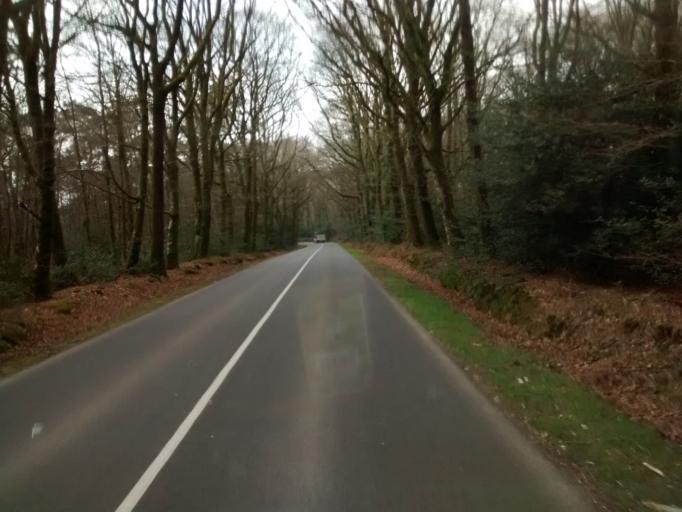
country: FR
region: Brittany
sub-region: Departement d'Ille-et-Vilaine
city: Paimpont
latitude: 48.0196
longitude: -2.1620
